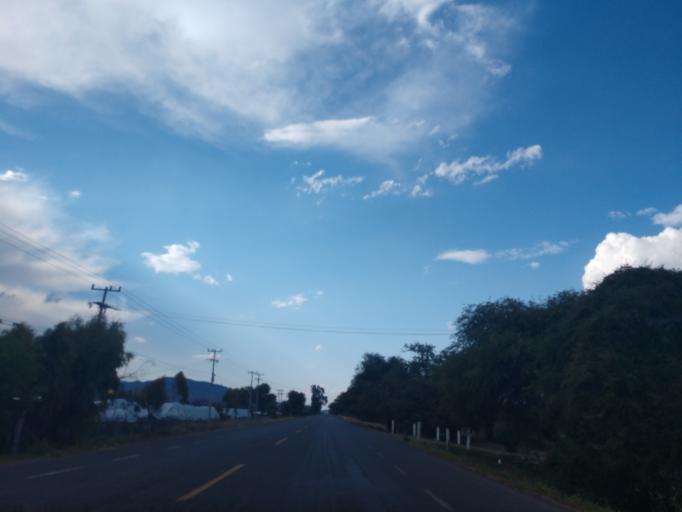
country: MX
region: Jalisco
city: Jocotepec
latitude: 20.2368
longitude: -103.4237
